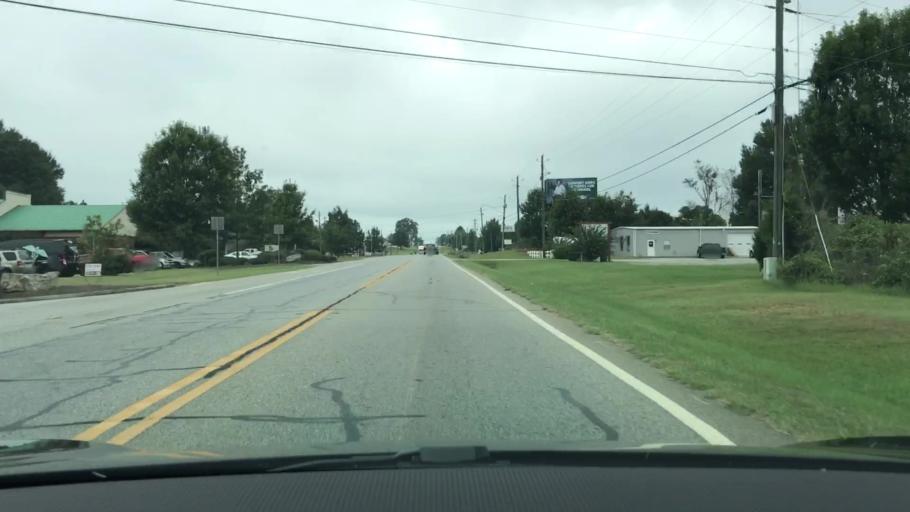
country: US
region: Georgia
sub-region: Oconee County
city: Watkinsville
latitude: 33.8525
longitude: -83.3981
